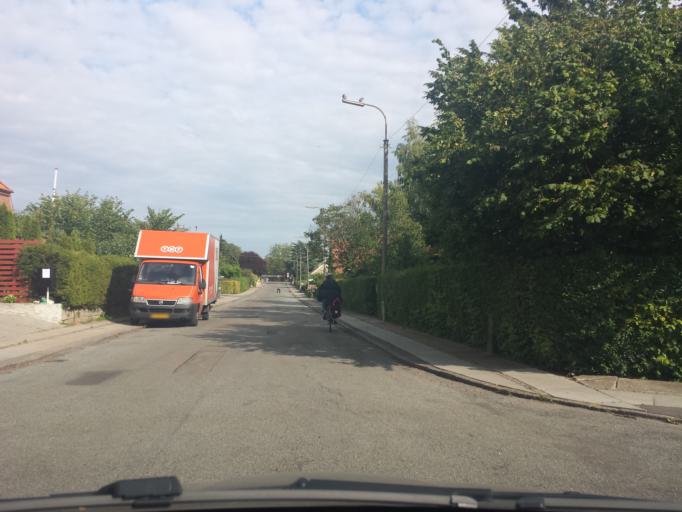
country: DK
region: Capital Region
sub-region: Herlev Kommune
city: Herlev
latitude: 55.7248
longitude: 12.4037
